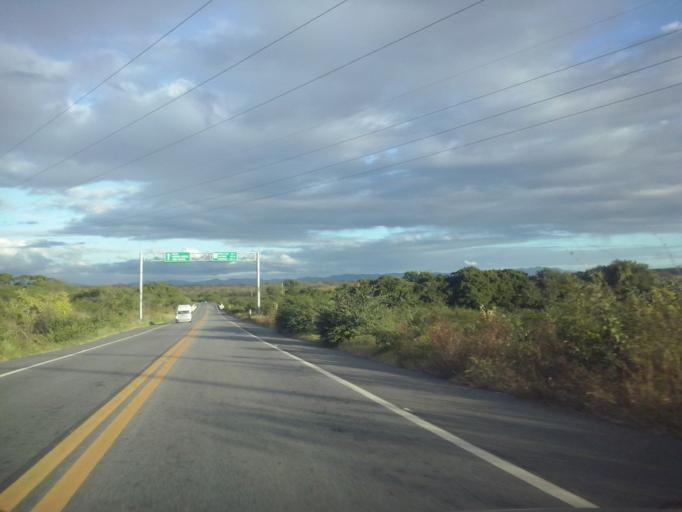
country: BR
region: Paraiba
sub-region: Patos
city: Patos
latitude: -6.9427
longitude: -37.4054
